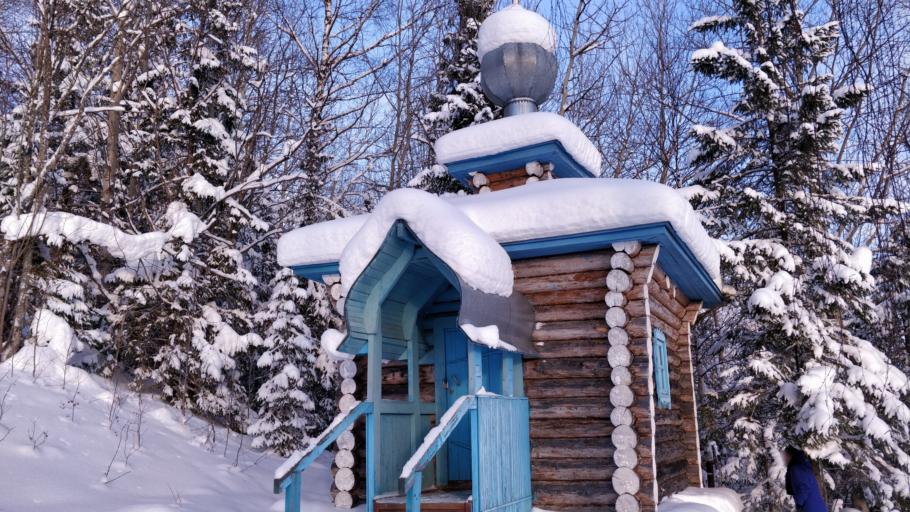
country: RU
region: Perm
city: Verkhnechusovskiye Gorodki
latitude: 58.2112
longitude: 57.0699
